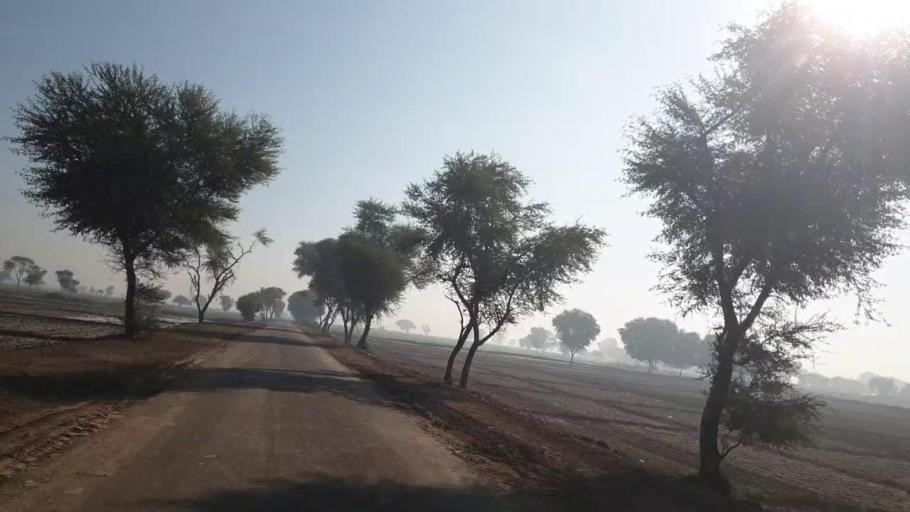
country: PK
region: Sindh
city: Dadu
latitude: 26.6728
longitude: 67.8208
